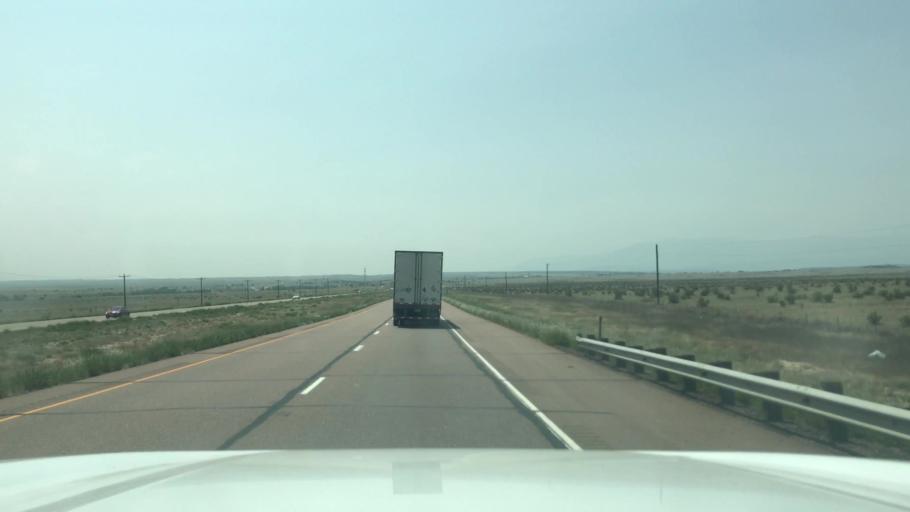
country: US
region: Colorado
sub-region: Pueblo County
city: Pueblo
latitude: 38.1434
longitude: -104.6593
